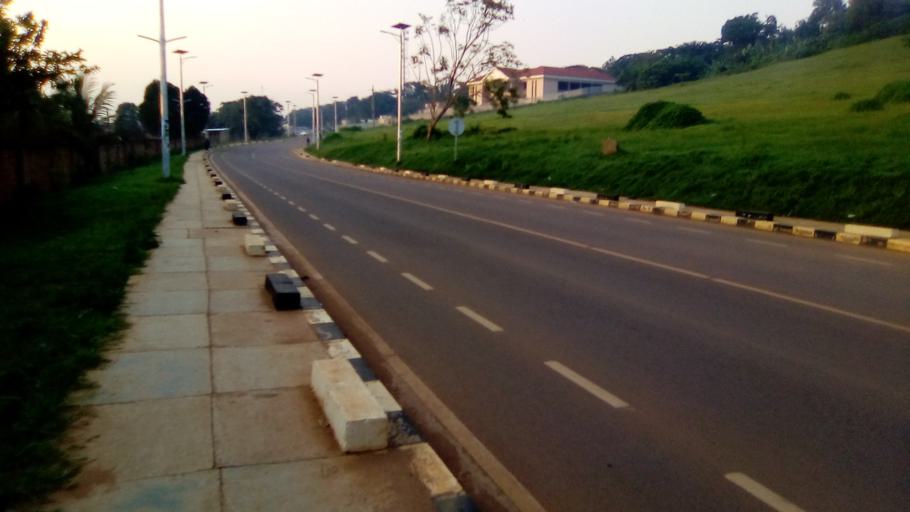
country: UG
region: Central Region
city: Masaka
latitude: -0.3372
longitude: 31.7379
